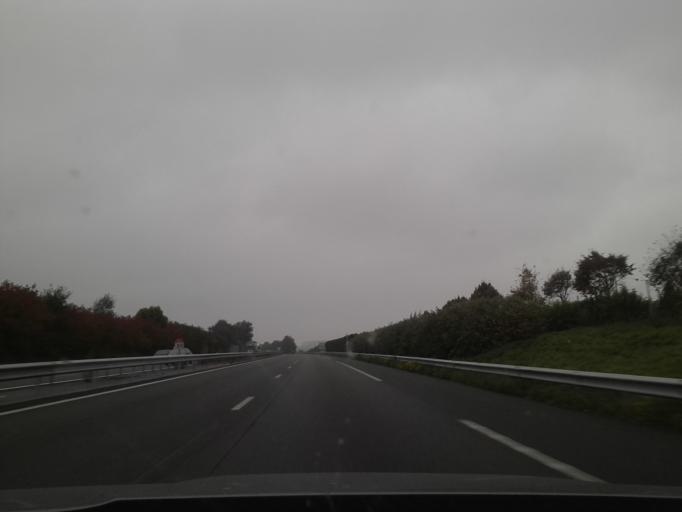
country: FR
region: Nord-Pas-de-Calais
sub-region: Departement du Nord
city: Neuville-Saint-Remy
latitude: 50.1909
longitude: 3.1981
